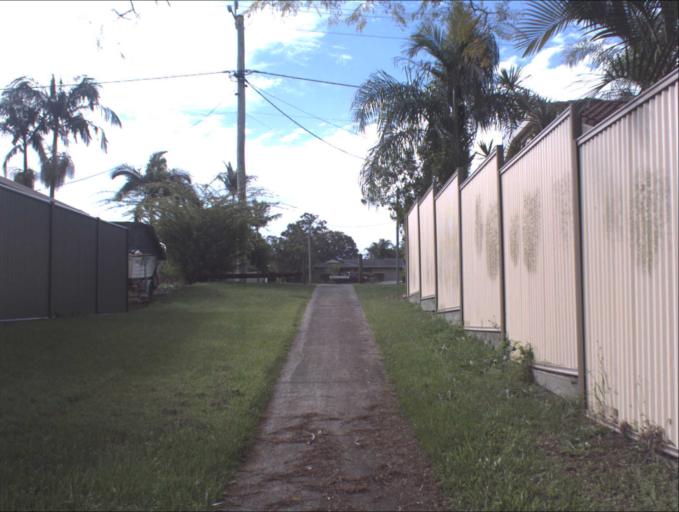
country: AU
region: Queensland
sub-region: Logan
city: Park Ridge South
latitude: -27.6858
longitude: 153.0373
